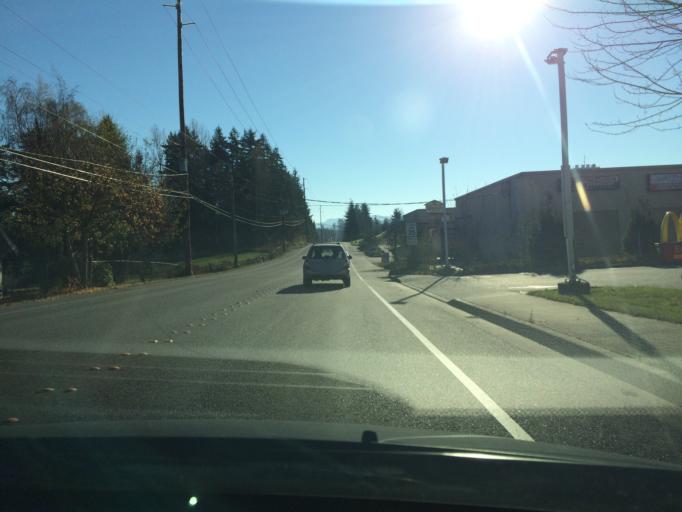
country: US
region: Washington
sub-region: Whatcom County
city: Bellingham
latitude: 48.7887
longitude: -122.4426
